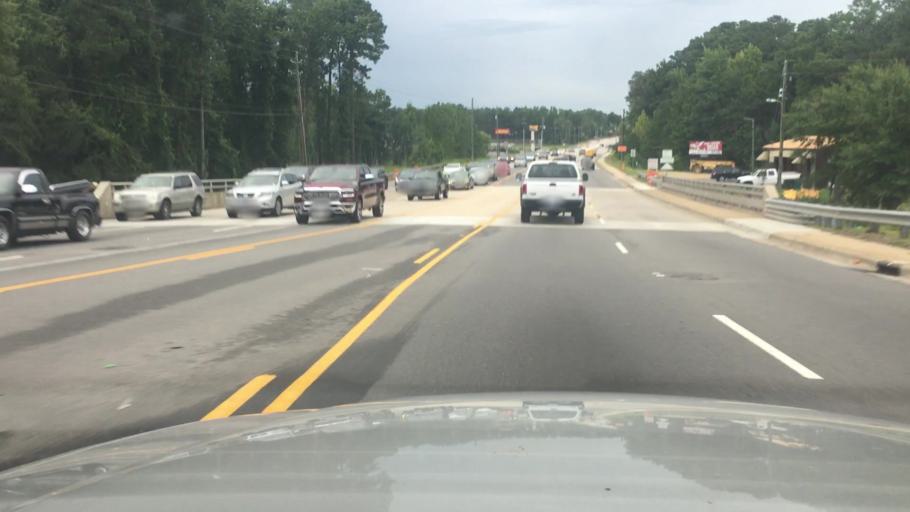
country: US
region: North Carolina
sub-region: Cumberland County
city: Hope Mills
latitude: 34.9869
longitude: -78.9653
